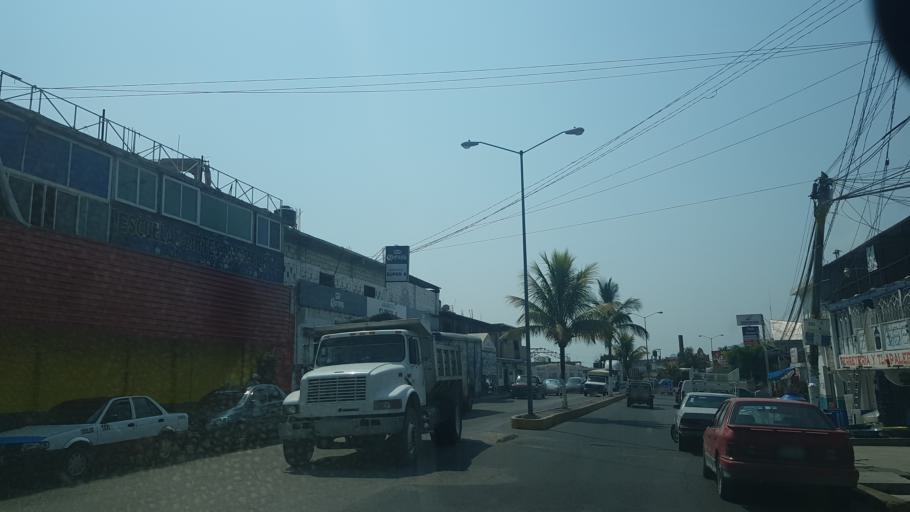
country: MX
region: Morelos
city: Amayuca
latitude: 18.7228
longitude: -98.7947
